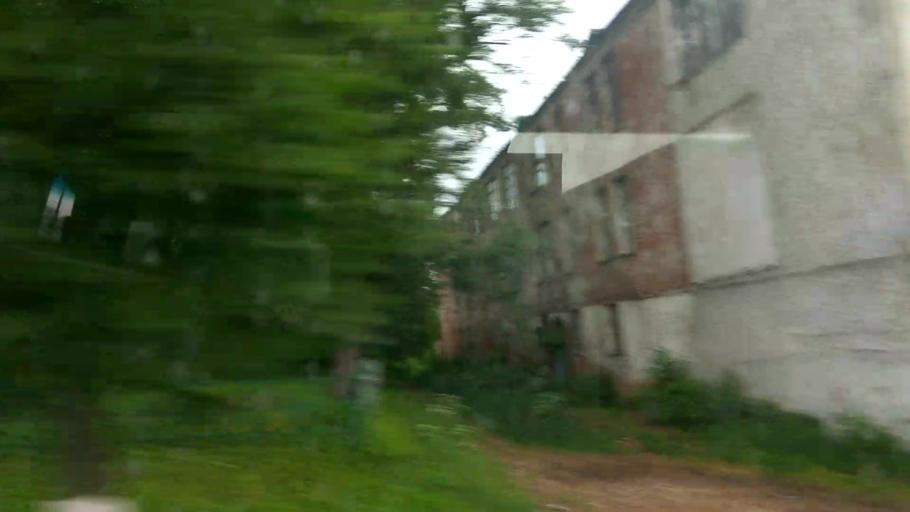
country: RU
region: Moskovskaya
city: Ozherel'ye
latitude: 54.8534
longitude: 38.2503
